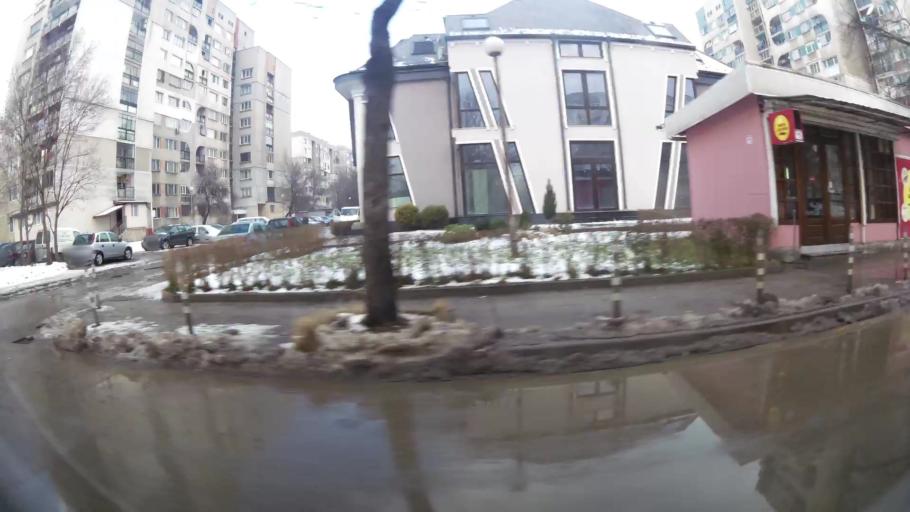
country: BG
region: Sofia-Capital
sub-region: Stolichna Obshtina
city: Sofia
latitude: 42.6985
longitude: 23.2862
